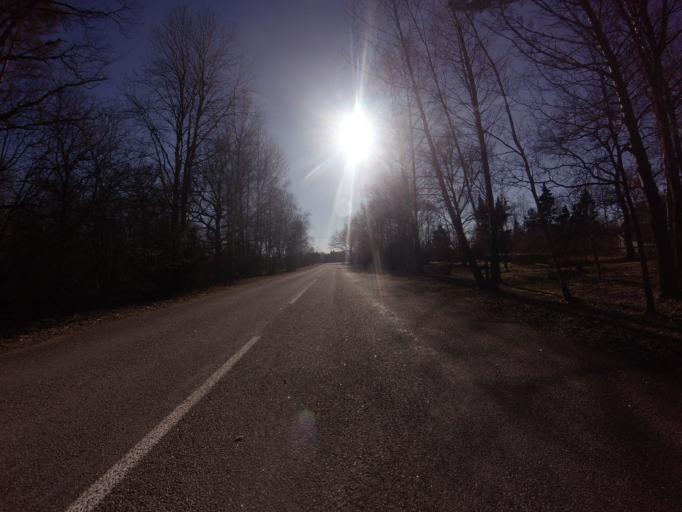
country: EE
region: Saare
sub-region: Kuressaare linn
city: Kuressaare
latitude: 58.4675
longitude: 22.2357
